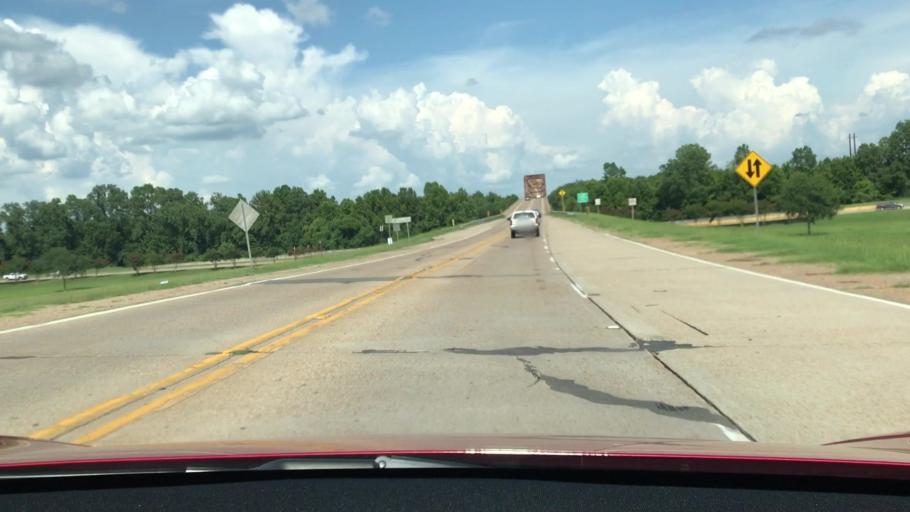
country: US
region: Louisiana
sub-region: Bossier Parish
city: Bossier City
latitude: 32.4588
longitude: -93.6854
